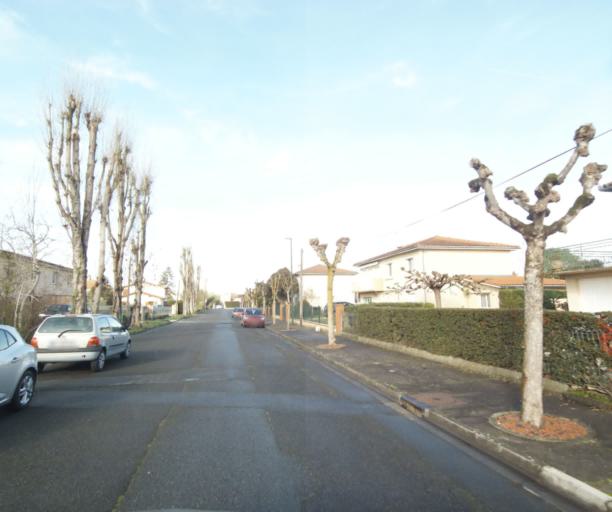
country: FR
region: Midi-Pyrenees
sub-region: Departement de la Haute-Garonne
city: Villemur-sur-Tarn
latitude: 43.8633
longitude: 1.4935
